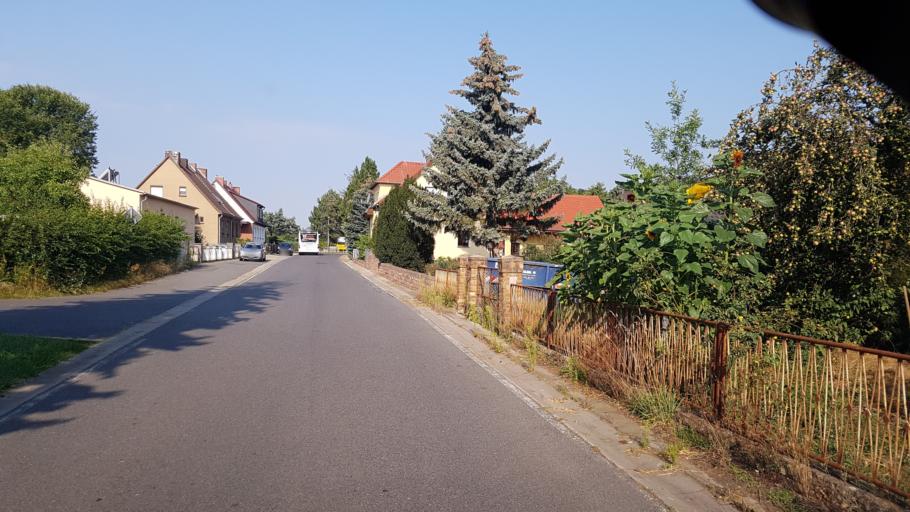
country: DE
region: Brandenburg
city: Drebkau
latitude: 51.6720
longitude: 14.2308
